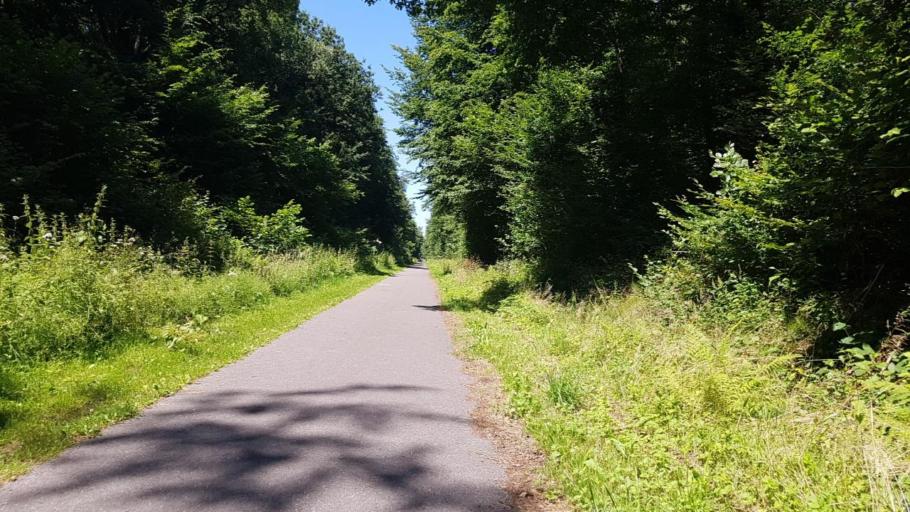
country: BE
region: Wallonia
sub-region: Province du Hainaut
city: Beaumont
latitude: 50.1621
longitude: 4.2502
